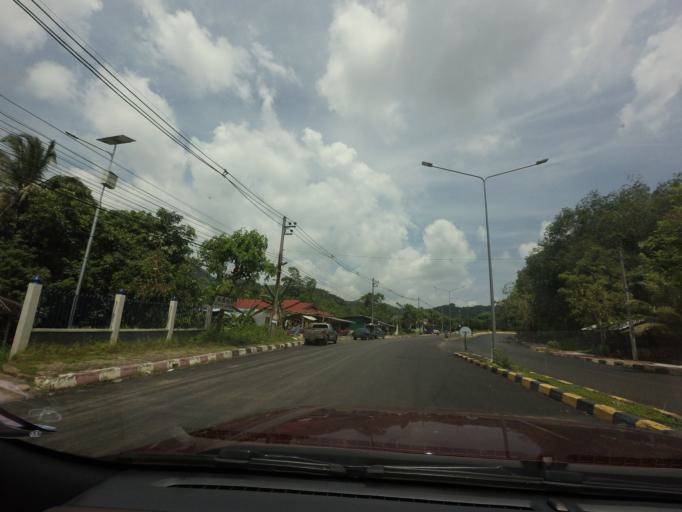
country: TH
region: Yala
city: Betong
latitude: 5.7508
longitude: 101.0415
